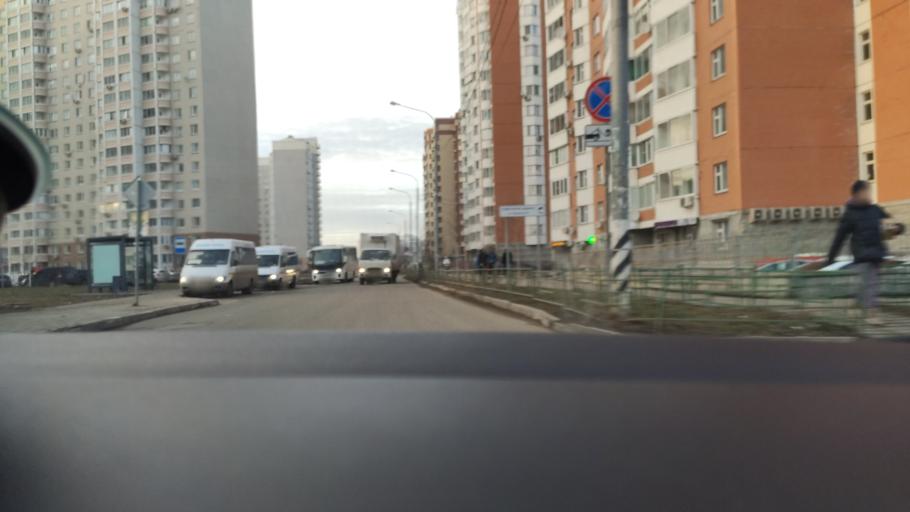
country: RU
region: Moskovskaya
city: Vidnoye
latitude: 55.5379
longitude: 37.7228
